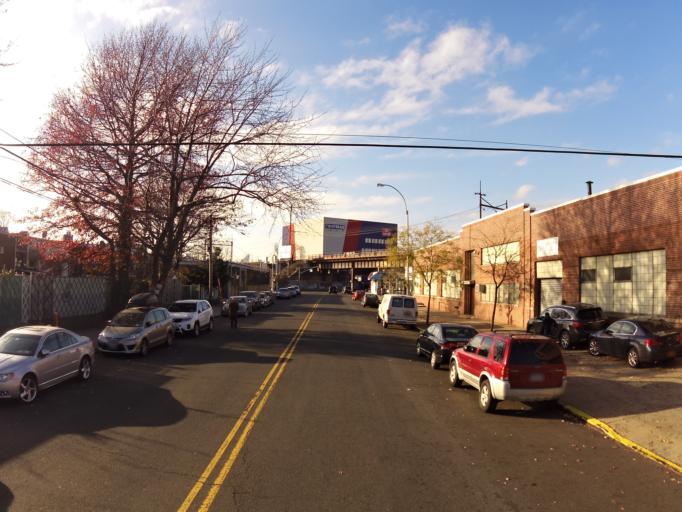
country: US
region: New York
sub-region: Queens County
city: Long Island City
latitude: 40.7512
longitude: -73.9083
